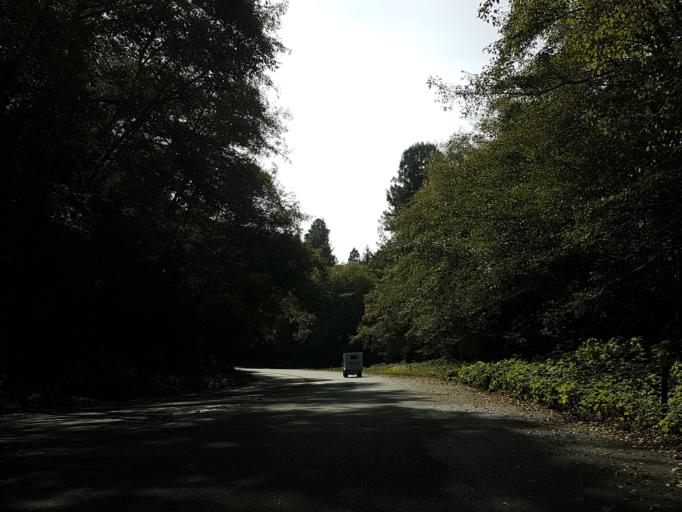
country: US
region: California
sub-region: Del Norte County
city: Bertsch-Oceanview
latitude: 41.4621
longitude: -124.0459
